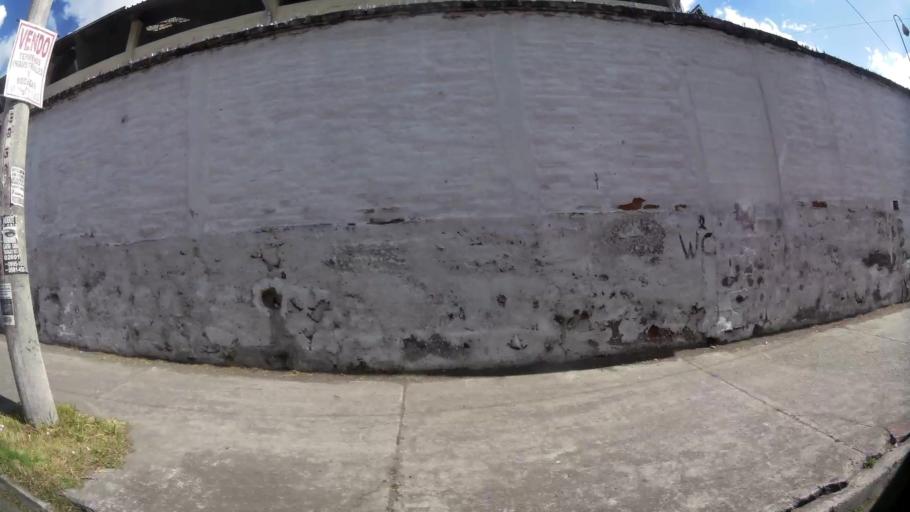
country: EC
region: Pichincha
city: Quito
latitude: -0.0999
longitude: -78.4734
